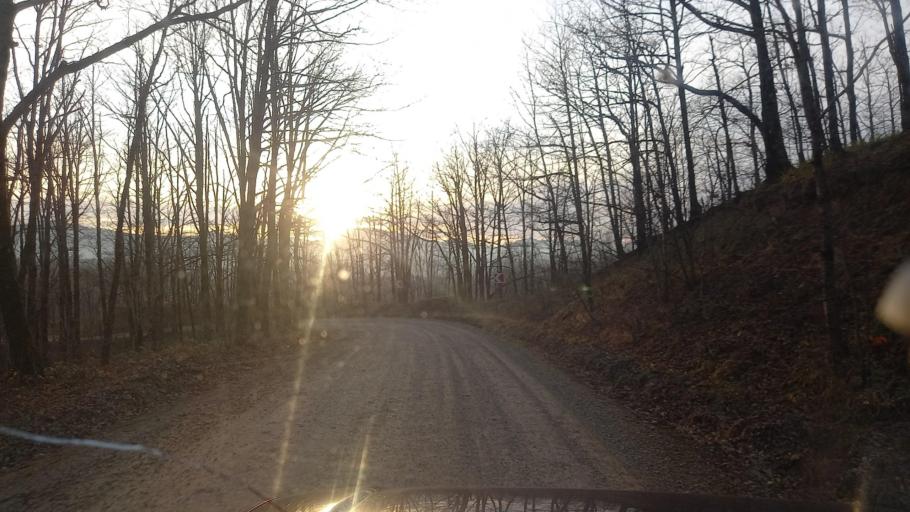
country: RU
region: Krasnodarskiy
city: Goryachiy Klyuch
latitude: 44.3693
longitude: 39.2196
